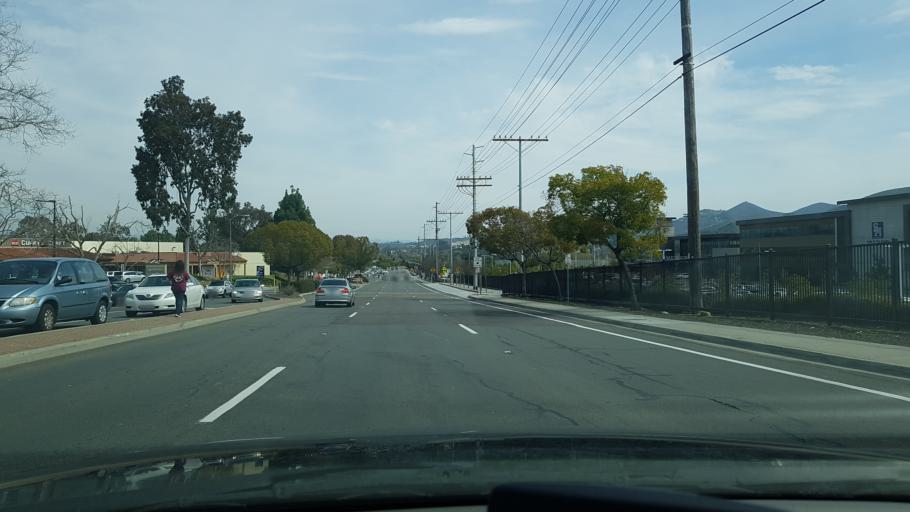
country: US
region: California
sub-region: San Diego County
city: Lake San Marcos
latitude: 33.1313
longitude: -117.2075
